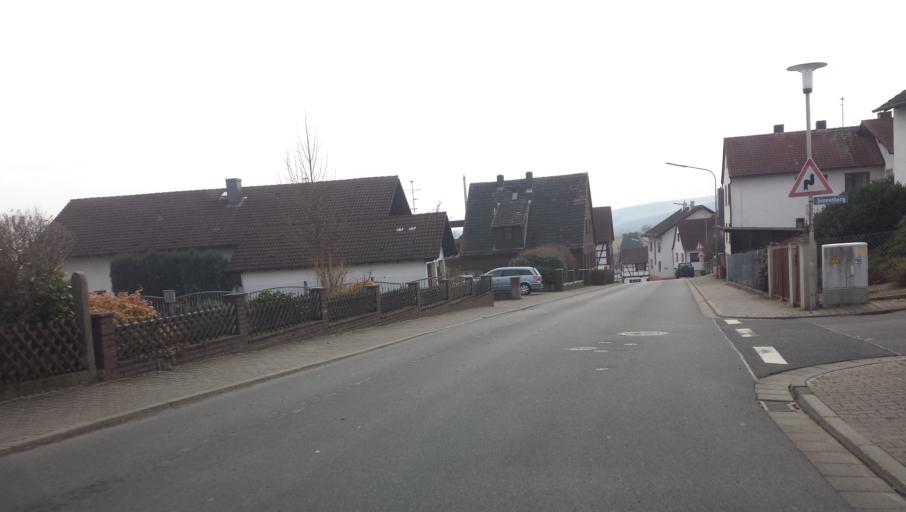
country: DE
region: Hesse
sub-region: Regierungsbezirk Darmstadt
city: Brensbach
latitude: 49.7816
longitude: 8.9387
